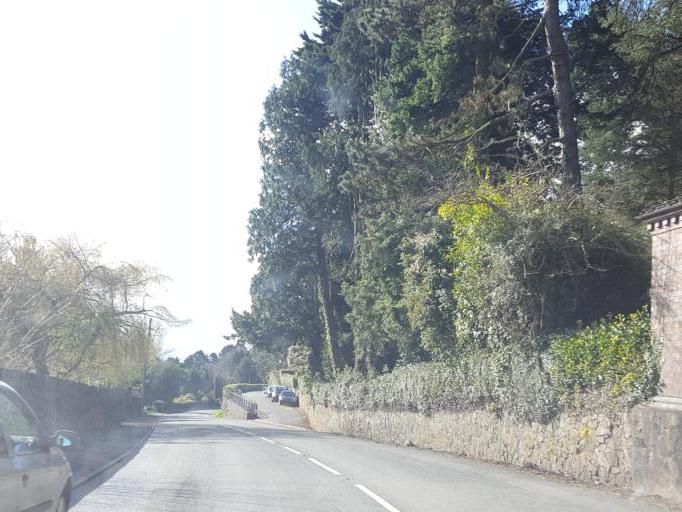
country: GB
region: England
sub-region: Worcestershire
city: Great Malvern
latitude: 52.0901
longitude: -2.3344
